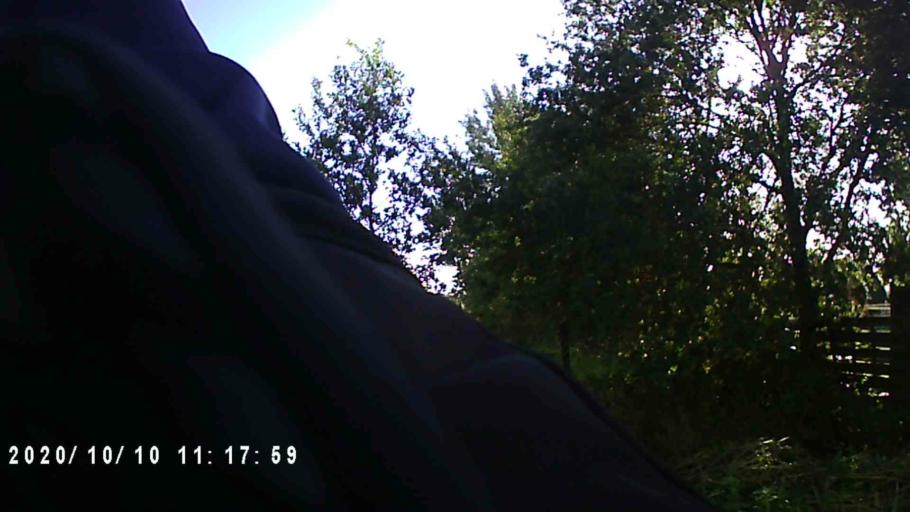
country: NL
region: Friesland
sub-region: Gemeente Smallingerland
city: Drachtstercompagnie
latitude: 53.0949
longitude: 6.1972
